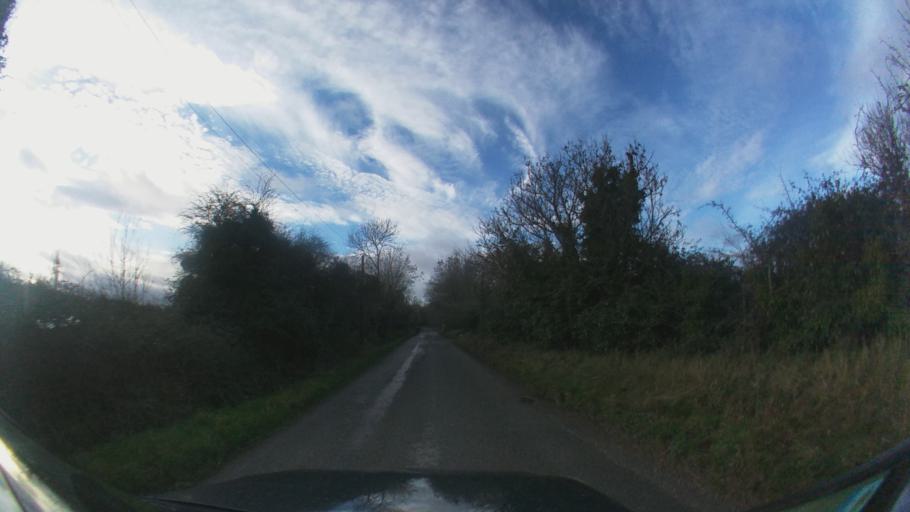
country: IE
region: Leinster
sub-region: Fingal County
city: Skerries
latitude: 53.5693
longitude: -6.1271
